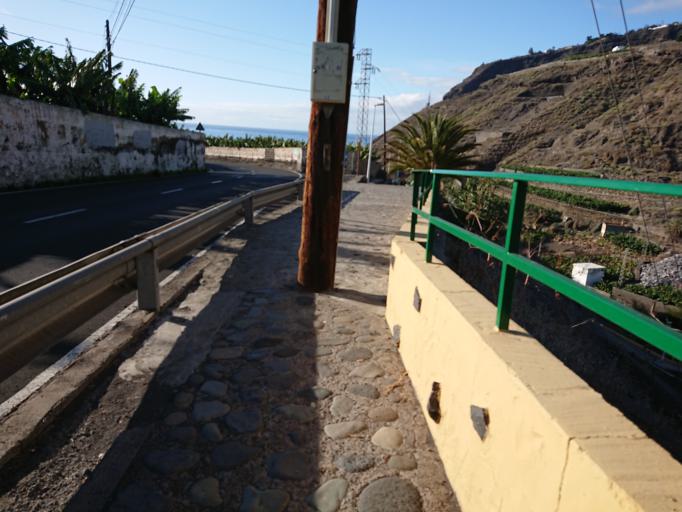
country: ES
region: Canary Islands
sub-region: Provincia de Santa Cruz de Tenerife
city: Tazacorte
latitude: 28.6462
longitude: -17.9380
